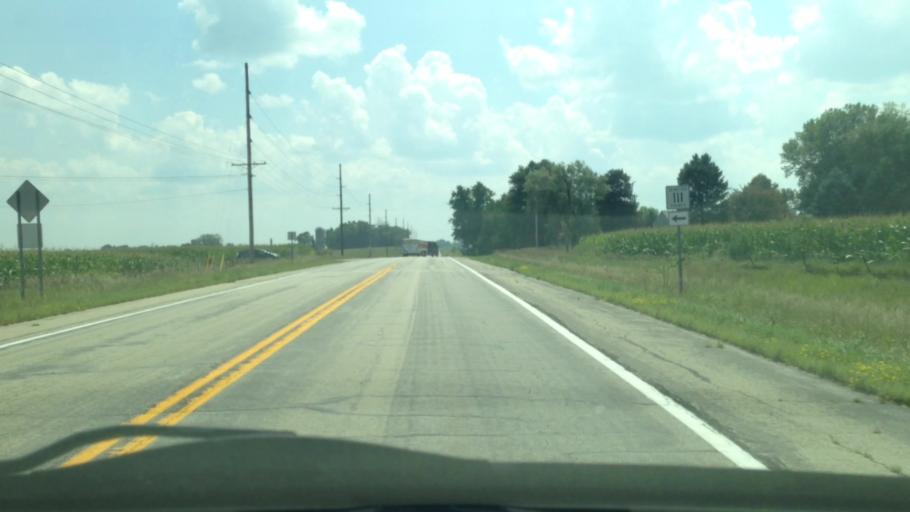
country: US
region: Minnesota
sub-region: Olmsted County
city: Rochester
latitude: 43.9429
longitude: -92.4087
